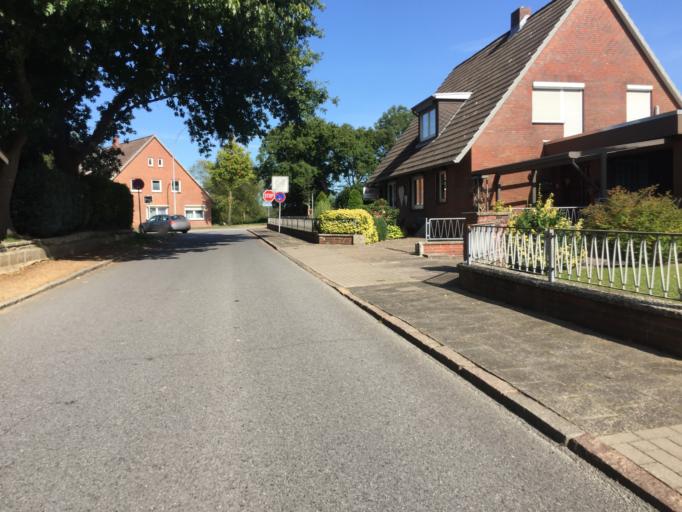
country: DE
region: Schleswig-Holstein
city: Itzehoe
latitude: 53.9109
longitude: 9.4926
